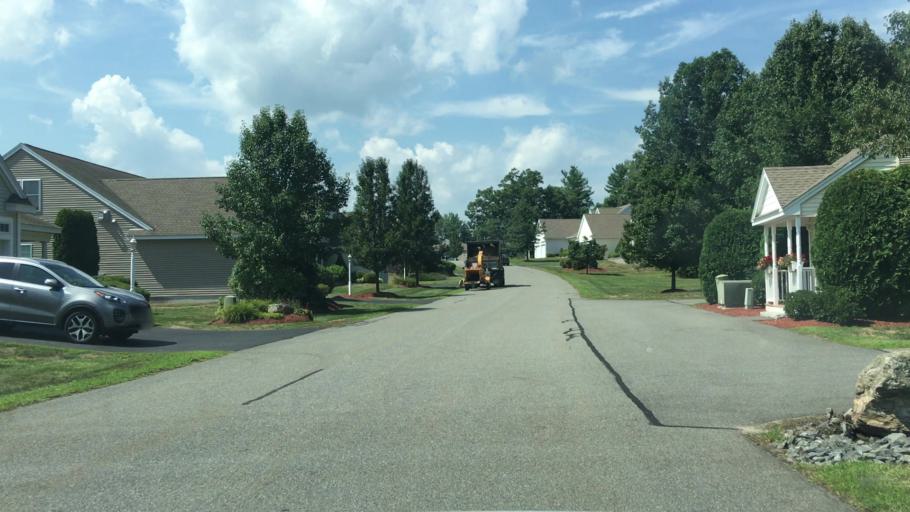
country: US
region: New Hampshire
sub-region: Rockingham County
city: Windham
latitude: 42.7876
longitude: -71.3579
